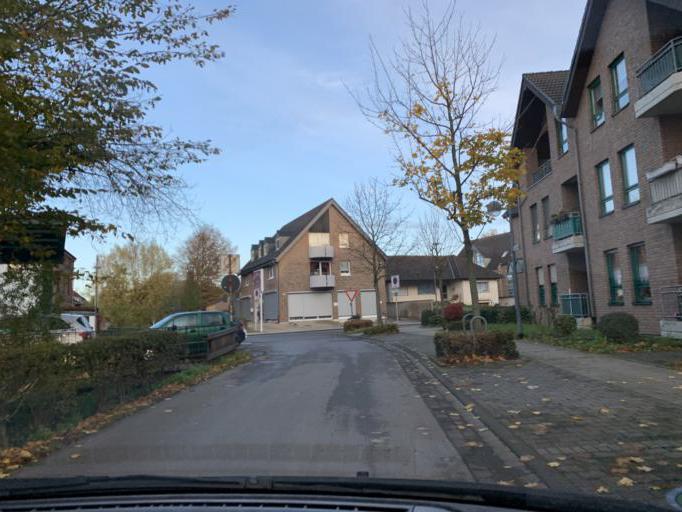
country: DE
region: North Rhine-Westphalia
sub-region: Regierungsbezirk Koln
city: Merzenich
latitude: 50.8271
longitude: 6.5238
